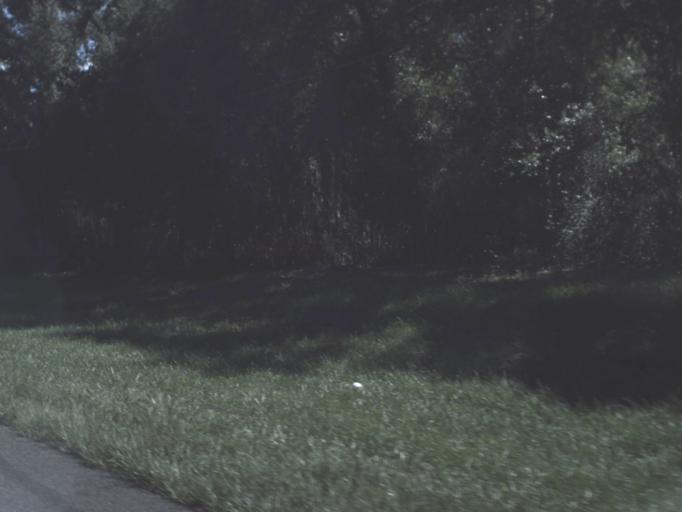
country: US
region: Florida
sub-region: Citrus County
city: Hernando
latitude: 28.9070
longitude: -82.3783
